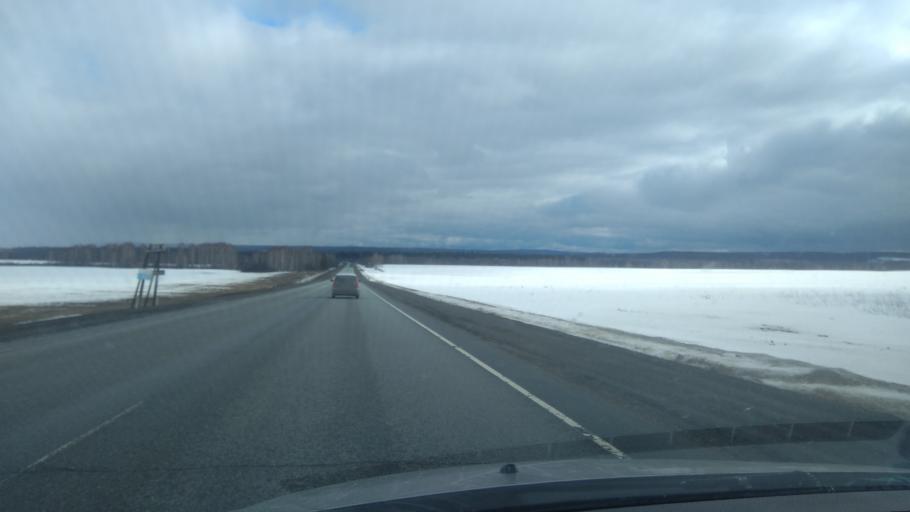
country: RU
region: Sverdlovsk
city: Ufimskiy
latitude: 56.7730
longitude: 58.0667
